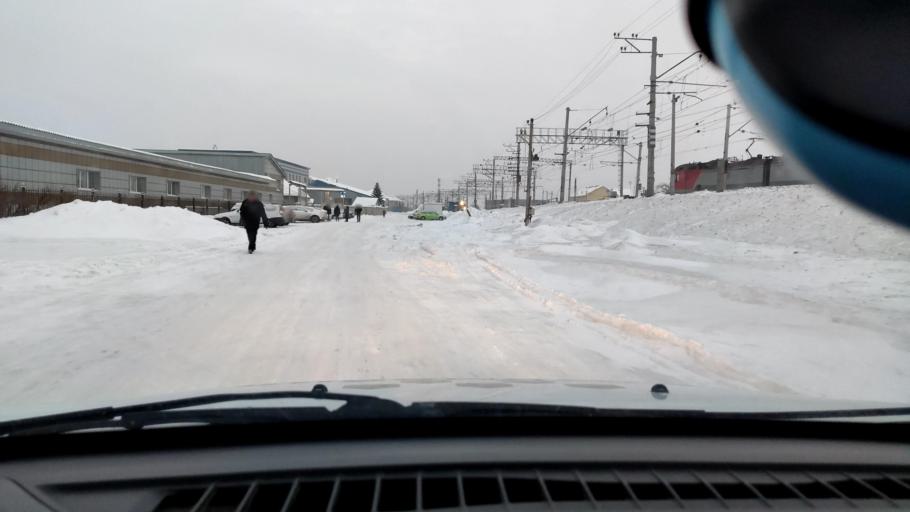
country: RU
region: Perm
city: Kondratovo
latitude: 58.0383
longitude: 56.1073
